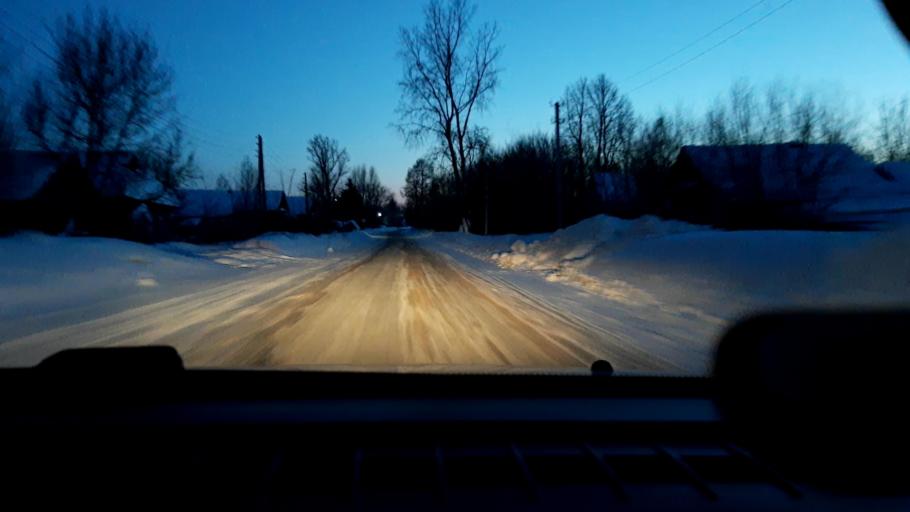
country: RU
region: Nizjnij Novgorod
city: Lyskovo
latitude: 56.1262
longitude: 45.3730
